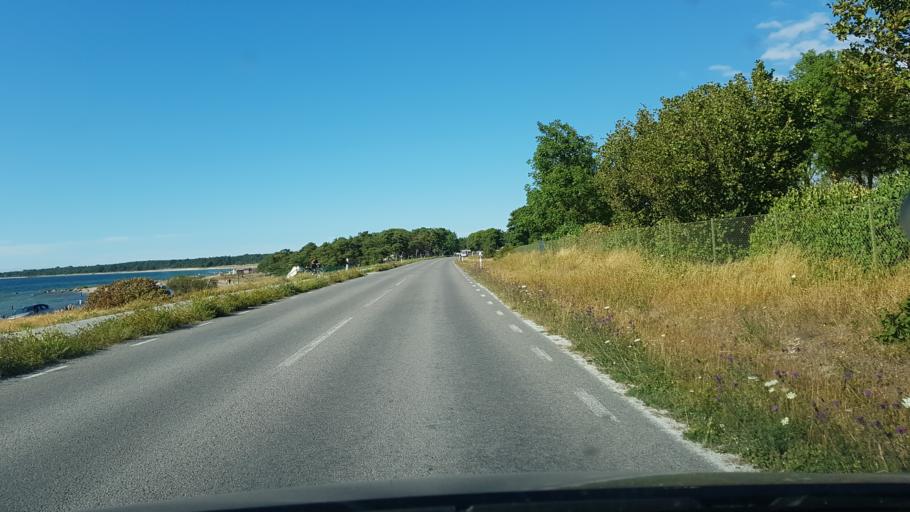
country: SE
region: Gotland
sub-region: Gotland
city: Klintehamn
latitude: 57.4805
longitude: 18.1265
